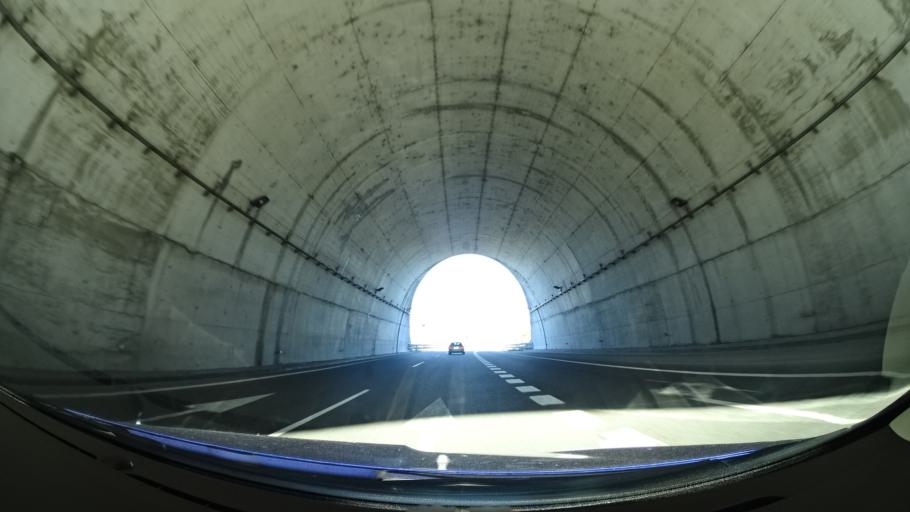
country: ES
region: Basque Country
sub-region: Provincia de Guipuzcoa
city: Astigarraga
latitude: 43.2755
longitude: -1.9590
